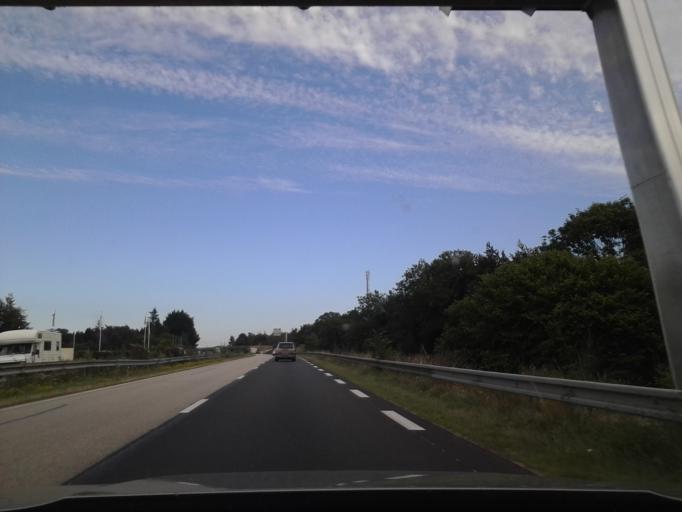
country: FR
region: Lower Normandy
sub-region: Departement de la Manche
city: Brix
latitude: 49.5363
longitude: -1.5364
